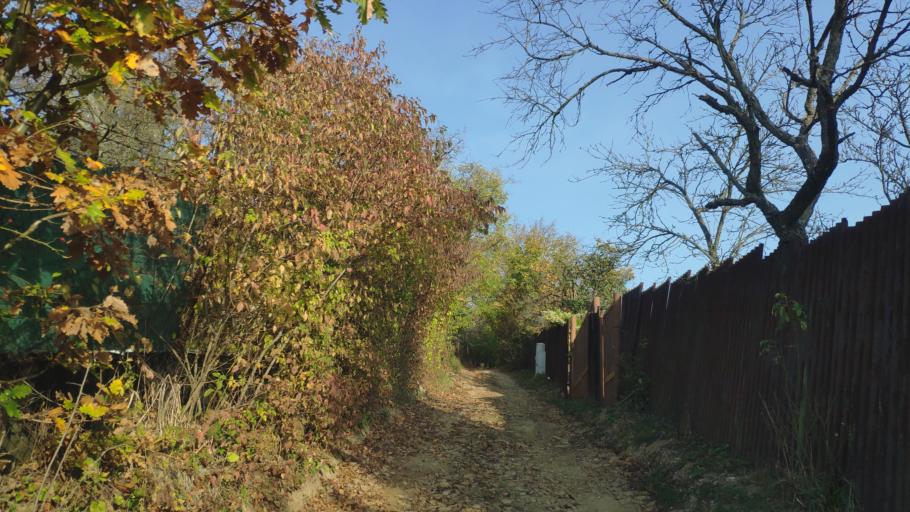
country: SK
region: Kosicky
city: Kosice
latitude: 48.7430
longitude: 21.2330
